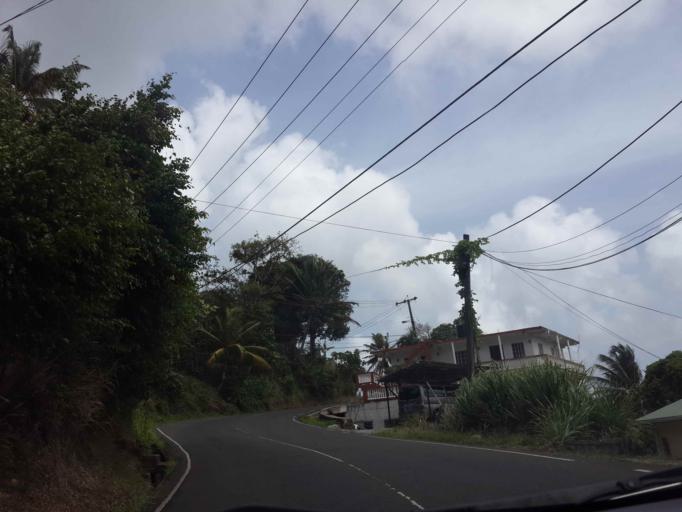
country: LC
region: Castries Quarter
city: Bisee
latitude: 14.0068
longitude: -60.9505
